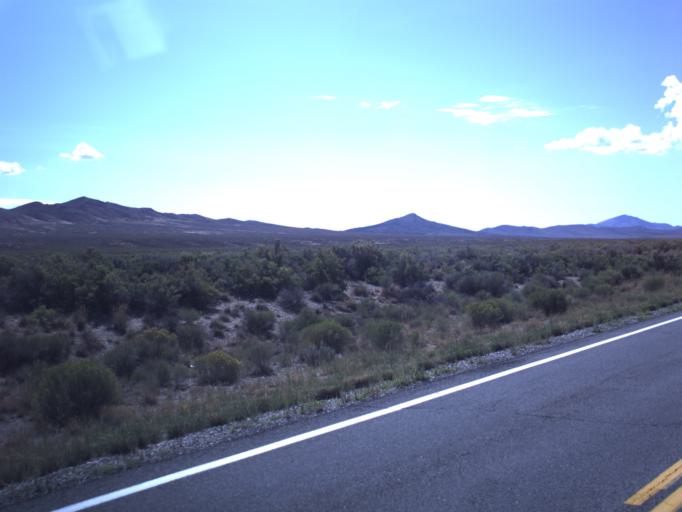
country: US
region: Utah
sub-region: Tooele County
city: Tooele
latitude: 40.1574
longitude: -112.4308
